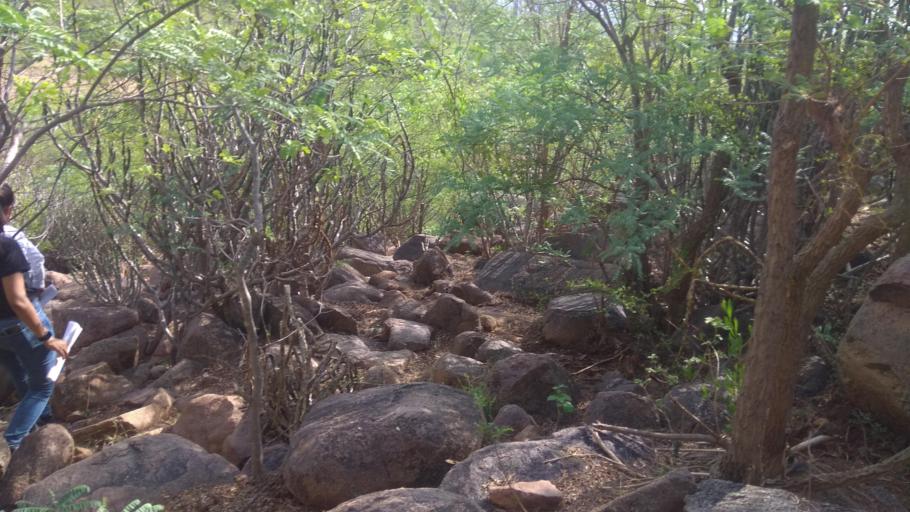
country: IN
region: Telangana
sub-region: Mahbubnagar
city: Farrukhnagar
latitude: 16.8897
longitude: 78.4811
